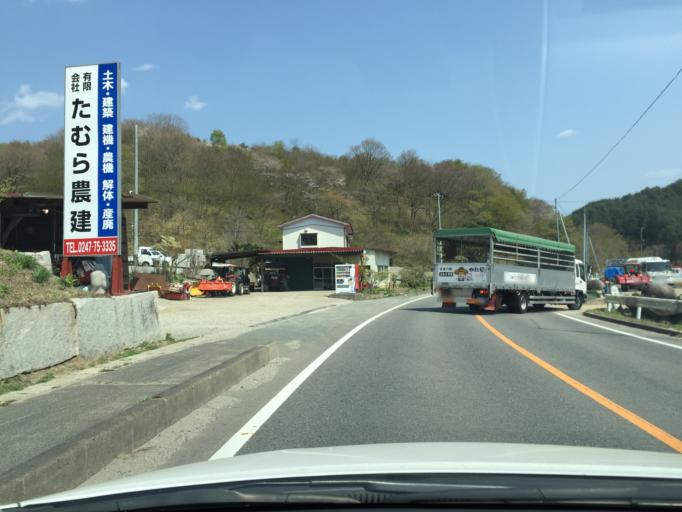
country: JP
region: Fukushima
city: Funehikimachi-funehiki
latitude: 37.4608
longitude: 140.7481
